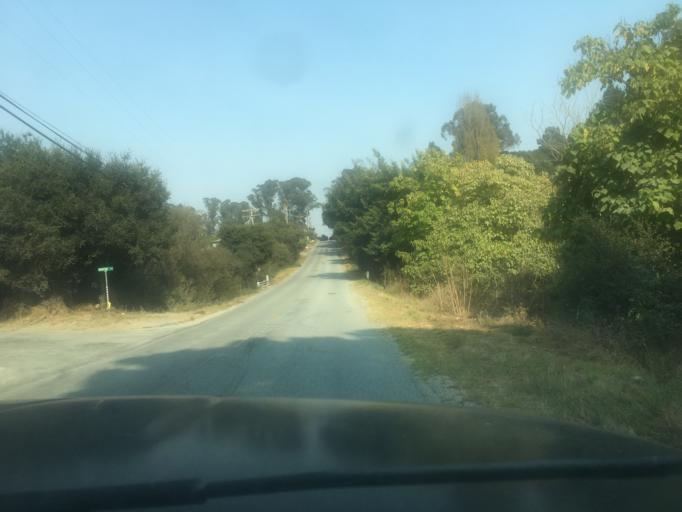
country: US
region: California
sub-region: Monterey County
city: Prunedale
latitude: 36.7770
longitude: -121.6605
